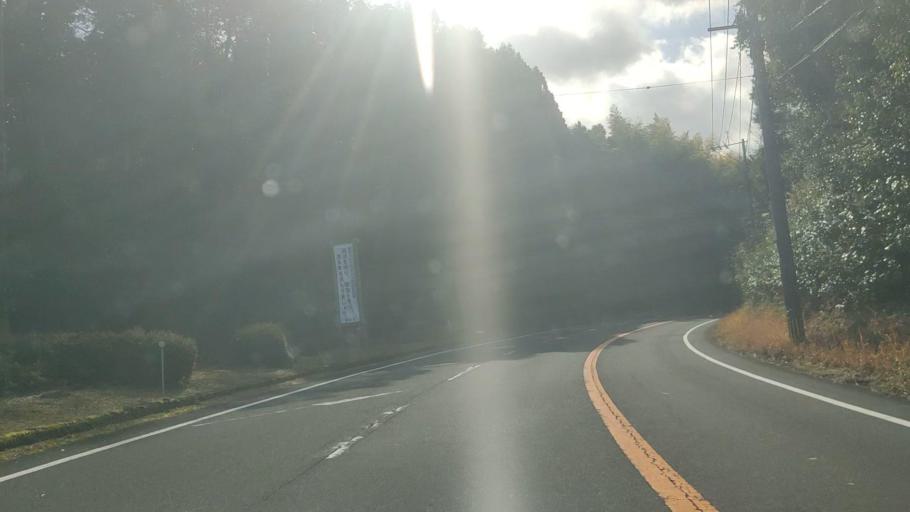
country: JP
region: Kagoshima
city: Okuchi-shinohara
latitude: 31.9291
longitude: 130.7038
